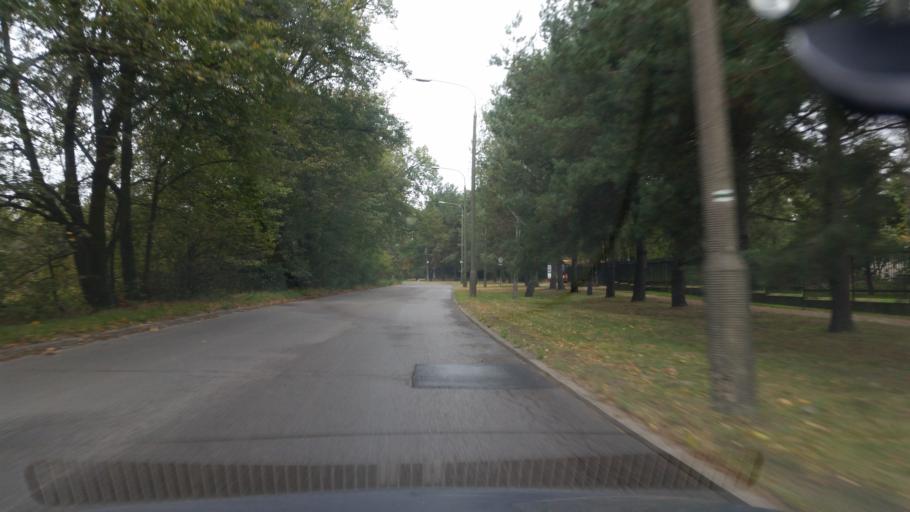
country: PL
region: Masovian Voivodeship
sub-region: Powiat piaseczynski
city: Konstancin-Jeziorna
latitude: 52.1047
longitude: 21.0939
